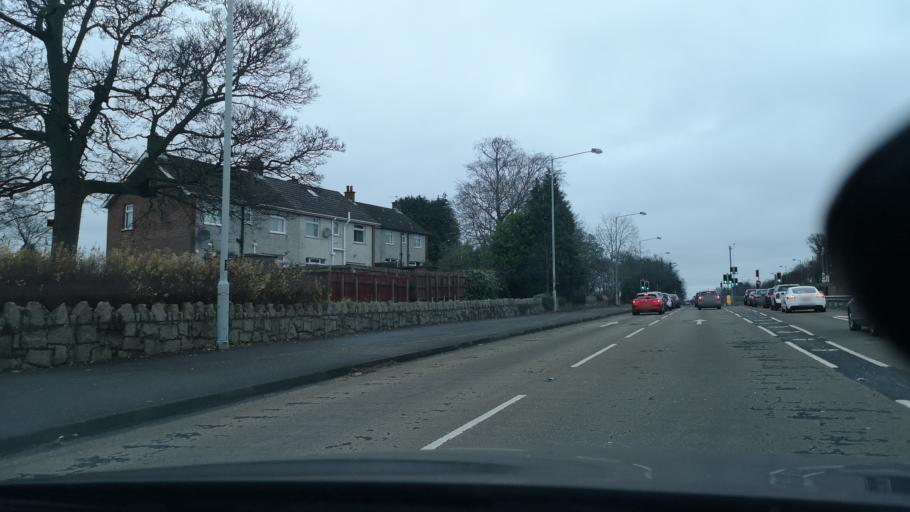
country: GB
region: Northern Ireland
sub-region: City of Belfast
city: Belfast
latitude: 54.5506
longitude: -5.9238
